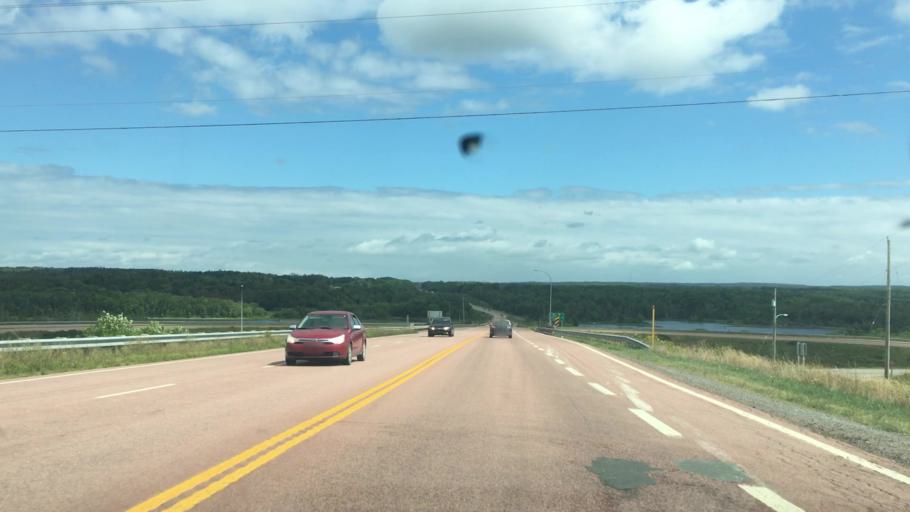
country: CA
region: Nova Scotia
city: Port Hawkesbury
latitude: 45.6135
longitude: -61.6292
